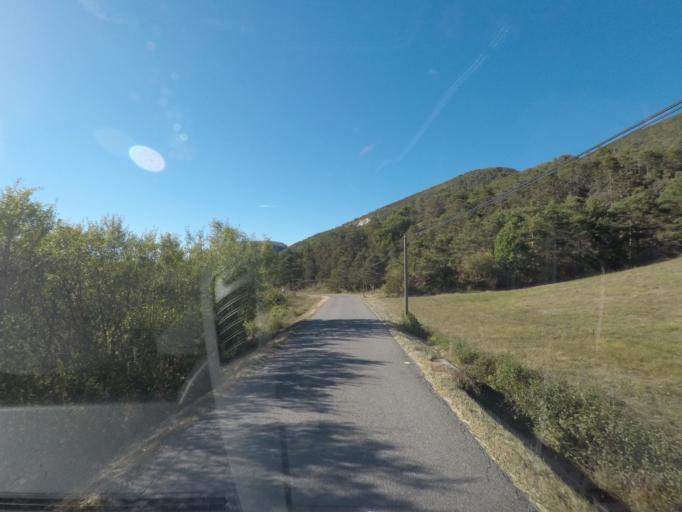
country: FR
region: Provence-Alpes-Cote d'Azur
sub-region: Departement des Hautes-Alpes
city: Serres
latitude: 44.4677
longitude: 5.4859
